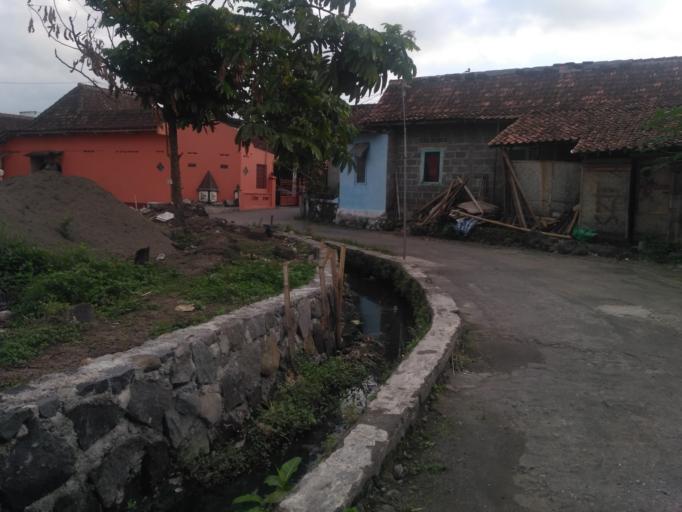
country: ID
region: Daerah Istimewa Yogyakarta
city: Melati
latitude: -7.7552
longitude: 110.3591
